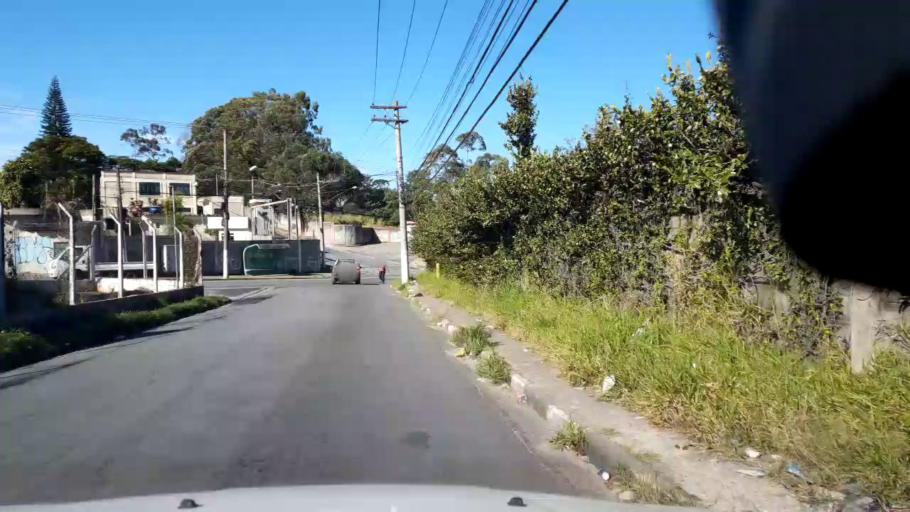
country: BR
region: Sao Paulo
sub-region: Ferraz De Vasconcelos
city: Ferraz de Vasconcelos
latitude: -23.5282
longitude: -46.3830
